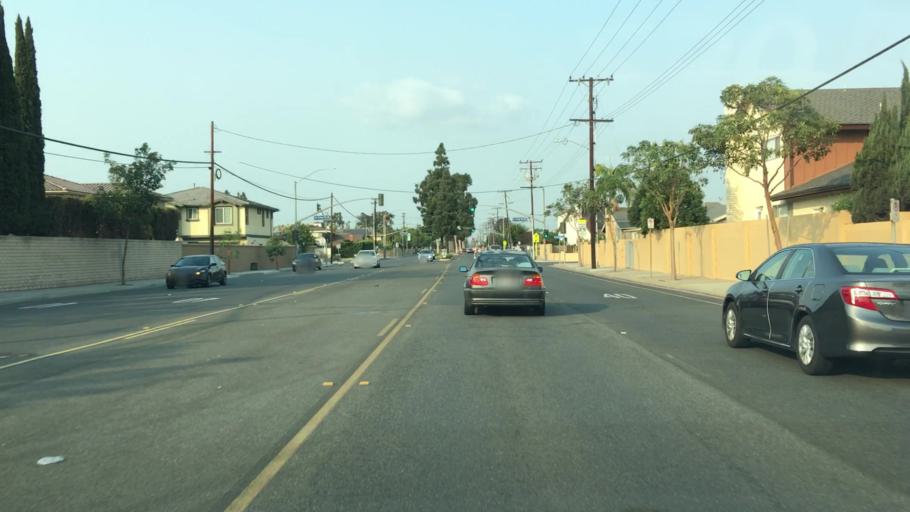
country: US
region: California
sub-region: Orange County
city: La Palma
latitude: 33.8421
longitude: -118.0459
